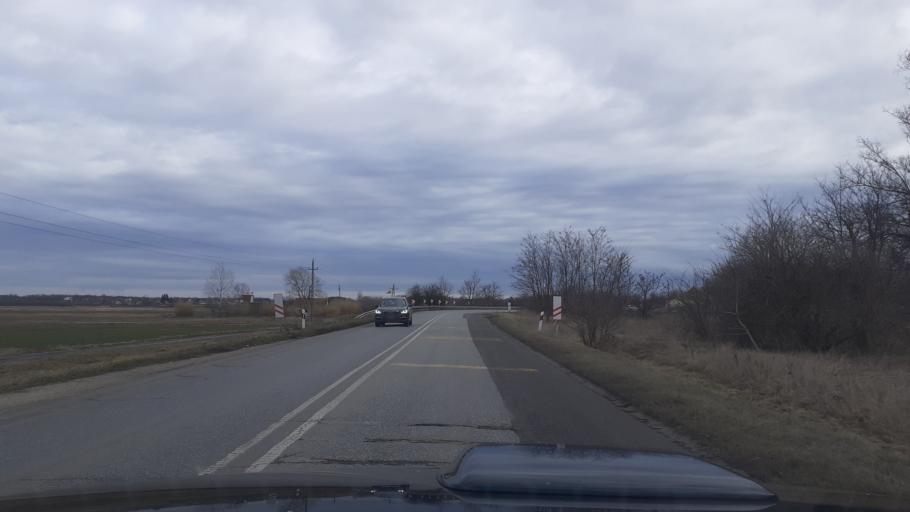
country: HU
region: Fejer
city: Seregelyes
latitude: 47.1227
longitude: 18.5596
